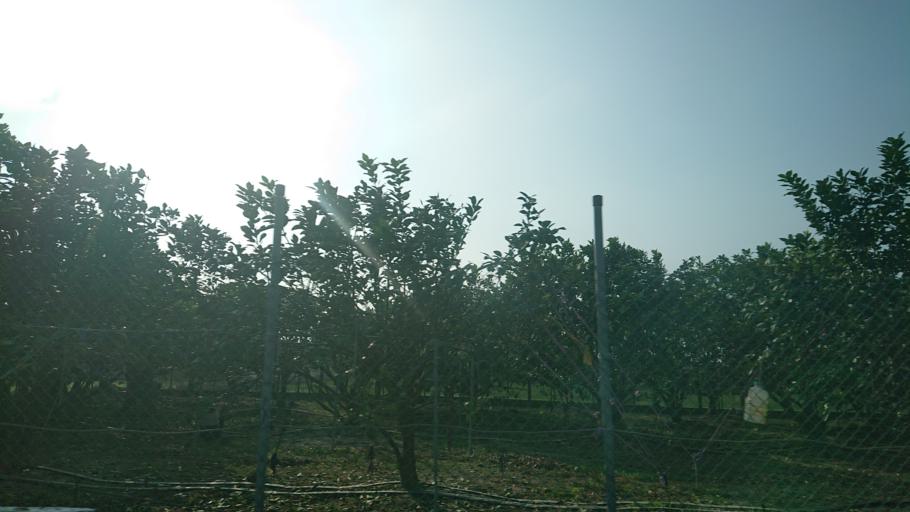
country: TW
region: Taiwan
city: Xinying
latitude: 23.1972
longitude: 120.2716
